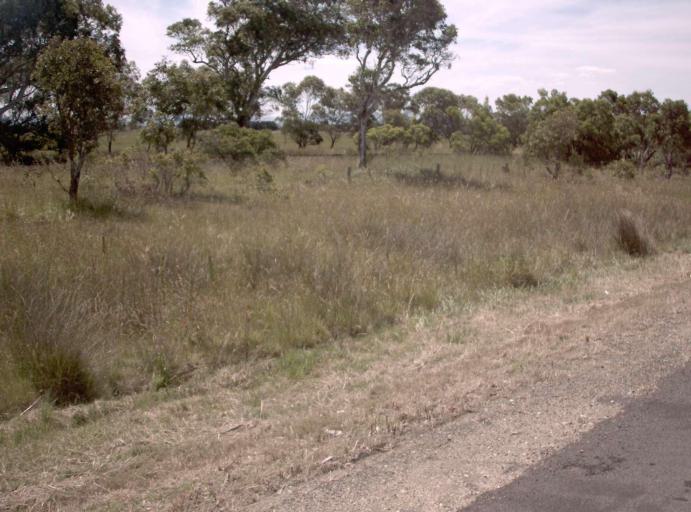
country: AU
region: Victoria
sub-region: Wellington
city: Sale
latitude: -38.0016
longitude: 147.0637
